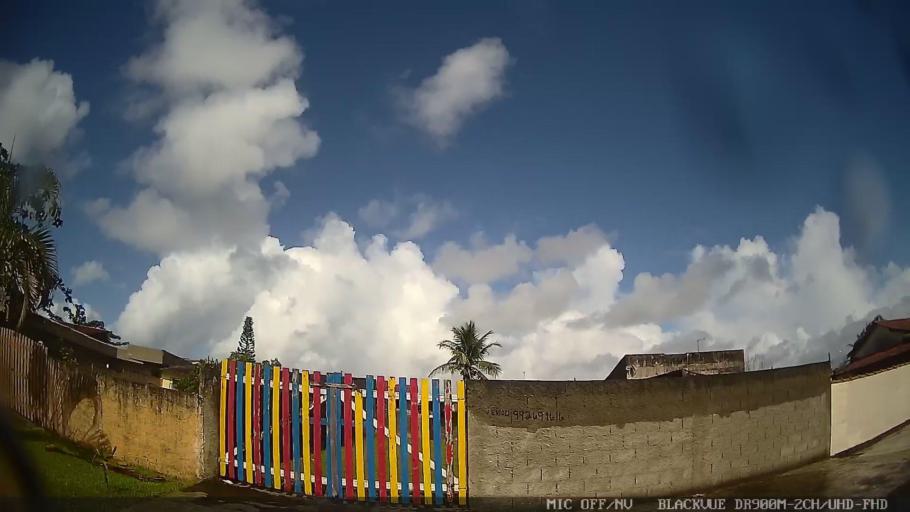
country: BR
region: Sao Paulo
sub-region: Itanhaem
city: Itanhaem
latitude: -24.2271
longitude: -46.8715
